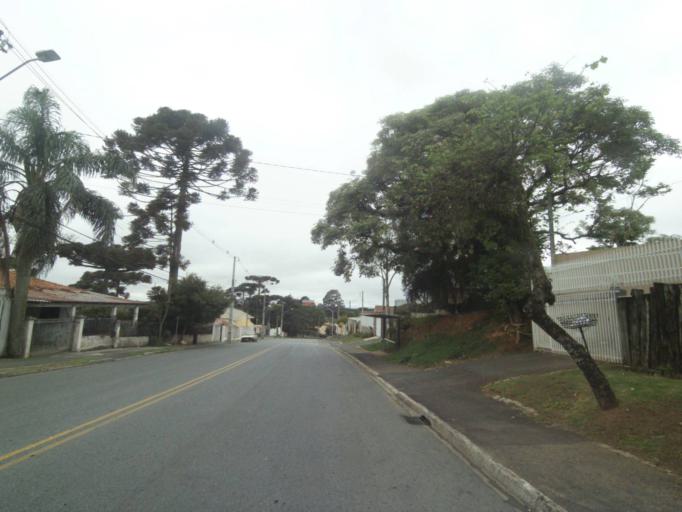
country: BR
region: Parana
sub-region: Curitiba
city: Curitiba
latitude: -25.3863
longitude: -49.2778
